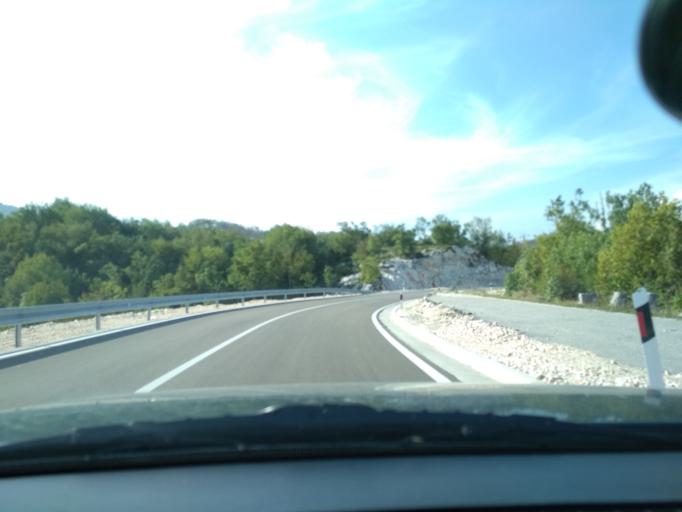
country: ME
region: Cetinje
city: Cetinje
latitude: 42.4237
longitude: 18.8739
